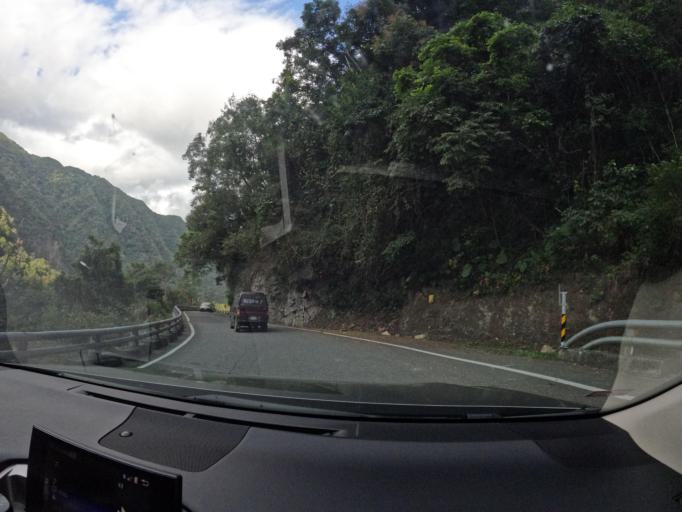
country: TW
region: Taiwan
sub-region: Taitung
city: Taitung
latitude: 23.1399
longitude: 121.0859
